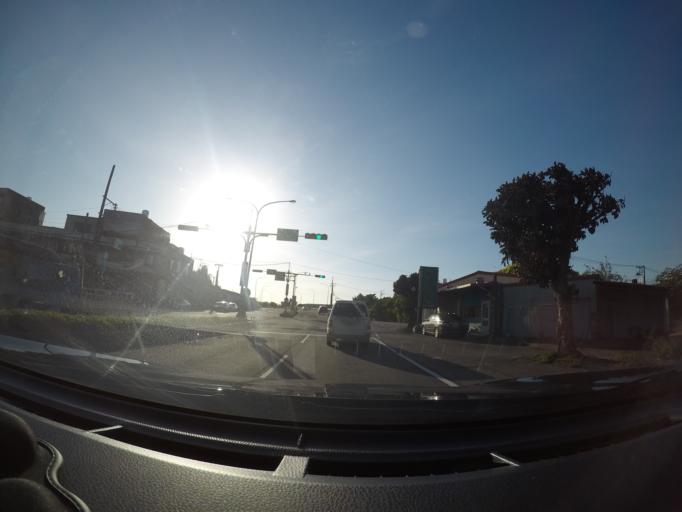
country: TW
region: Taiwan
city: Taoyuan City
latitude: 25.0798
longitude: 121.2110
